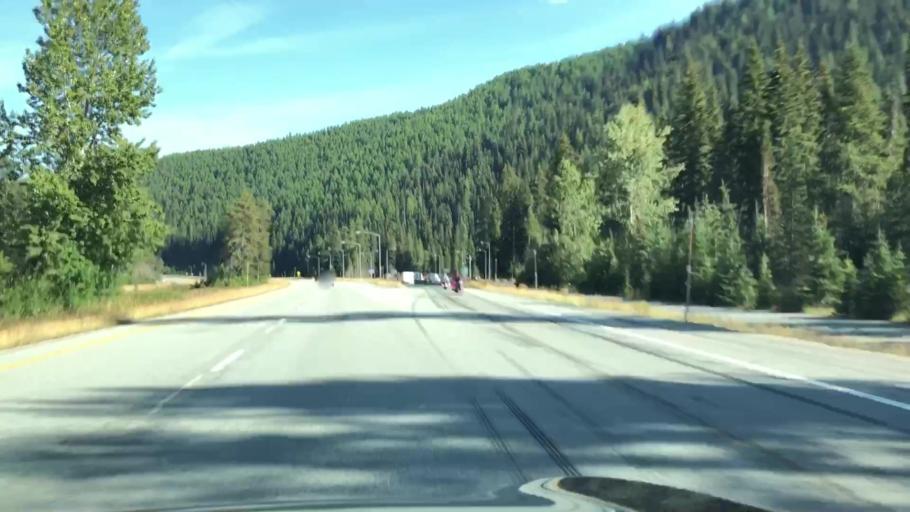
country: US
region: Idaho
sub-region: Shoshone County
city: Wallace
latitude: 47.4215
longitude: -115.6323
